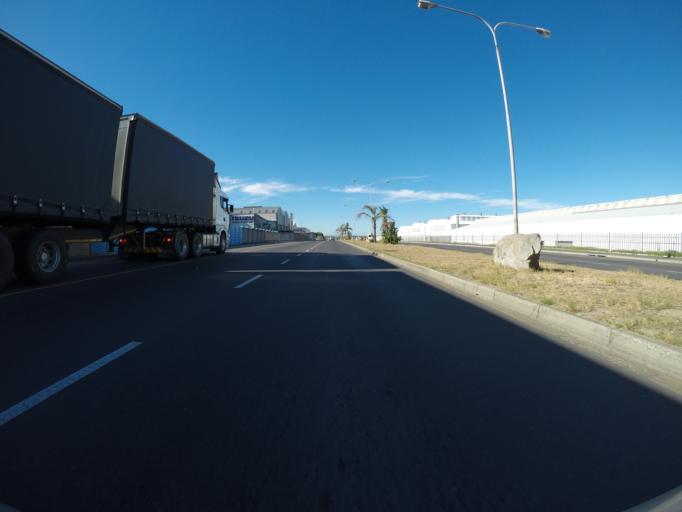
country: ZA
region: Western Cape
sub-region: City of Cape Town
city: Kraaifontein
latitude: -33.9015
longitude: 18.6694
